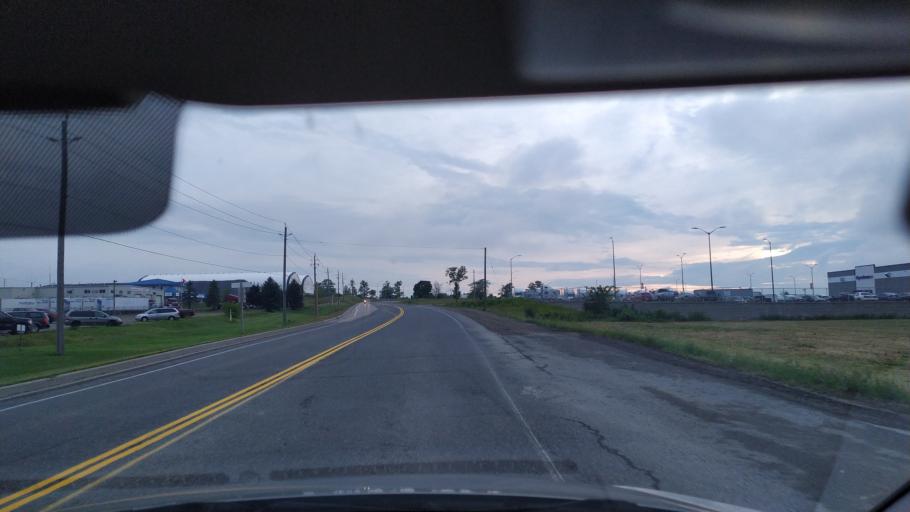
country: CA
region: Ontario
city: Kitchener
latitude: 43.3334
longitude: -80.4360
